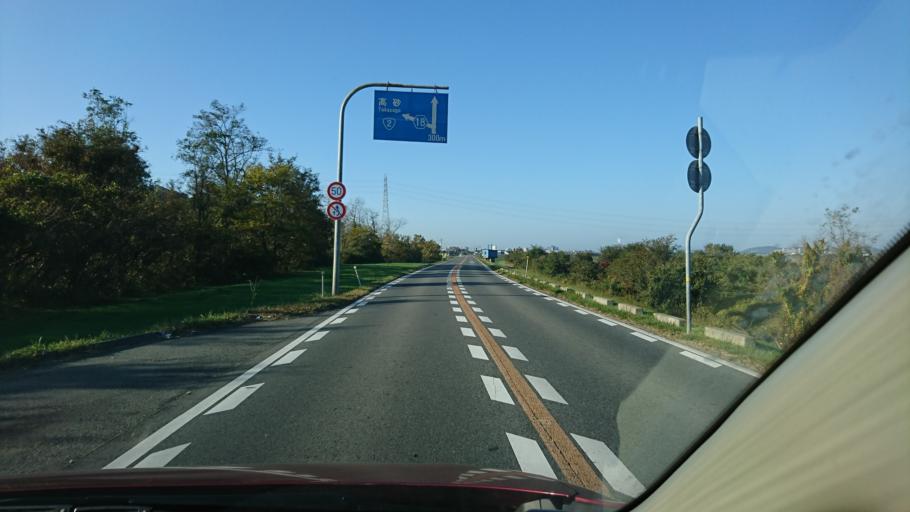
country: JP
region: Hyogo
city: Kakogawacho-honmachi
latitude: 34.7850
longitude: 134.8649
